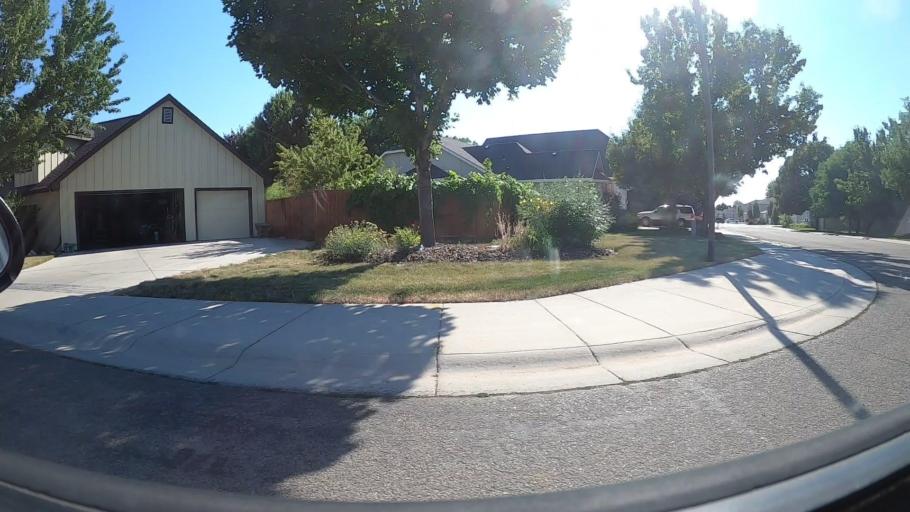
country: US
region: Idaho
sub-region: Ada County
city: Meridian
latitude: 43.6317
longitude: -116.3674
